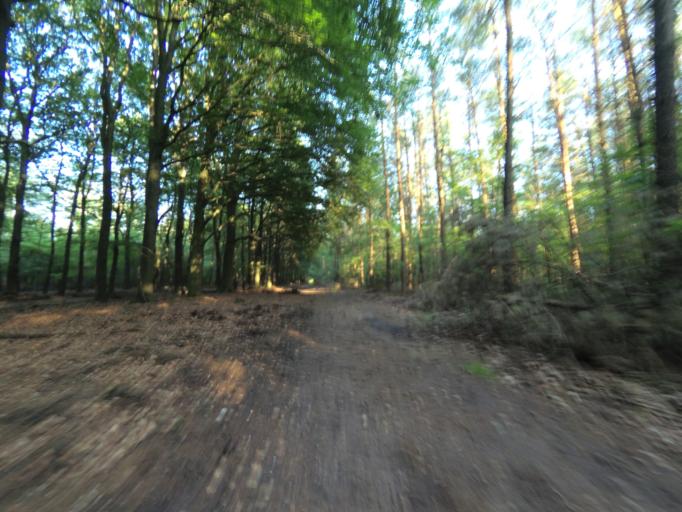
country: NL
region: Gelderland
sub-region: Gemeente Apeldoorn
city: Beekbergen
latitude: 52.1558
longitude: 5.8857
